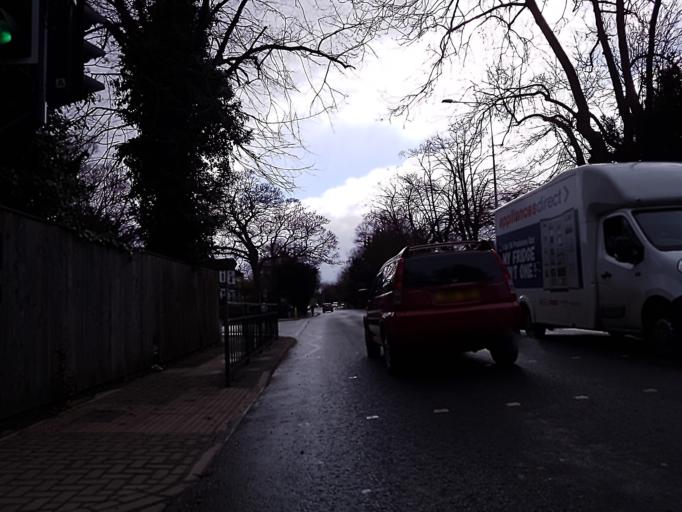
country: GB
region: England
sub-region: North East Lincolnshire
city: Grimbsy
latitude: 53.5599
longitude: -0.0921
